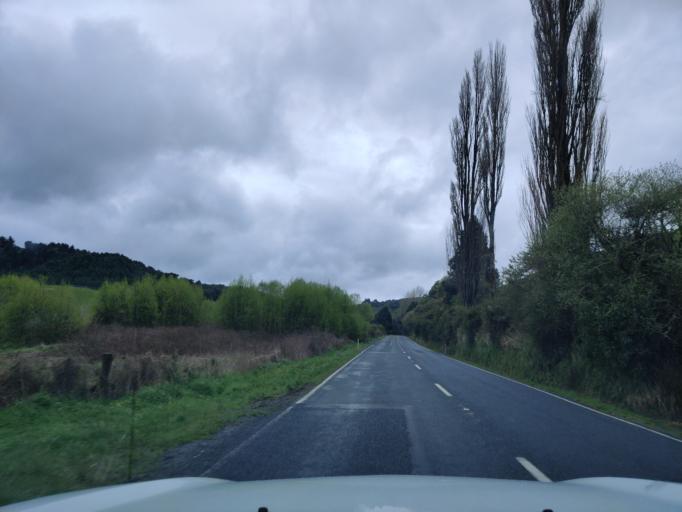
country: NZ
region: Waikato
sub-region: Otorohanga District
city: Otorohanga
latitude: -38.5609
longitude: 175.1968
